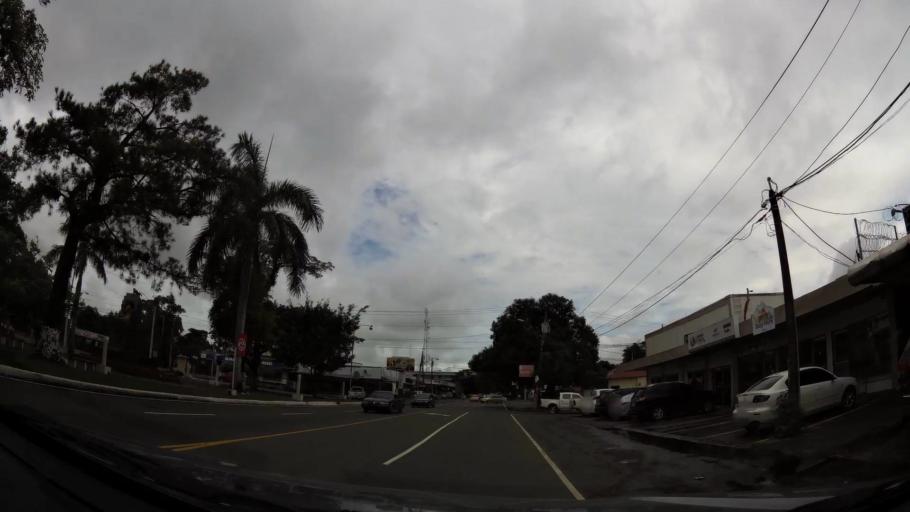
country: PA
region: Chiriqui
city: David
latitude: 8.4384
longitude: -82.4240
